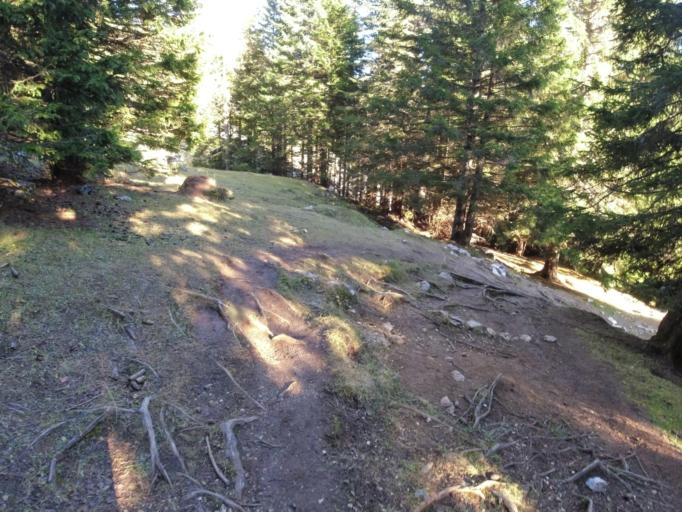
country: AT
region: Carinthia
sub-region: Politischer Bezirk Volkermarkt
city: Gallizien
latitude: 46.5026
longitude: 14.5100
